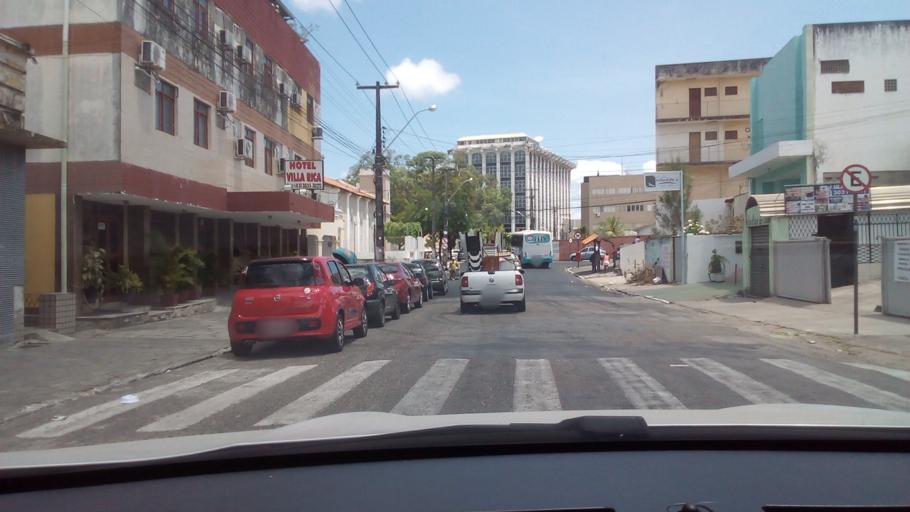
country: BR
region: Paraiba
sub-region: Joao Pessoa
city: Joao Pessoa
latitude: -7.1229
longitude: -34.8861
